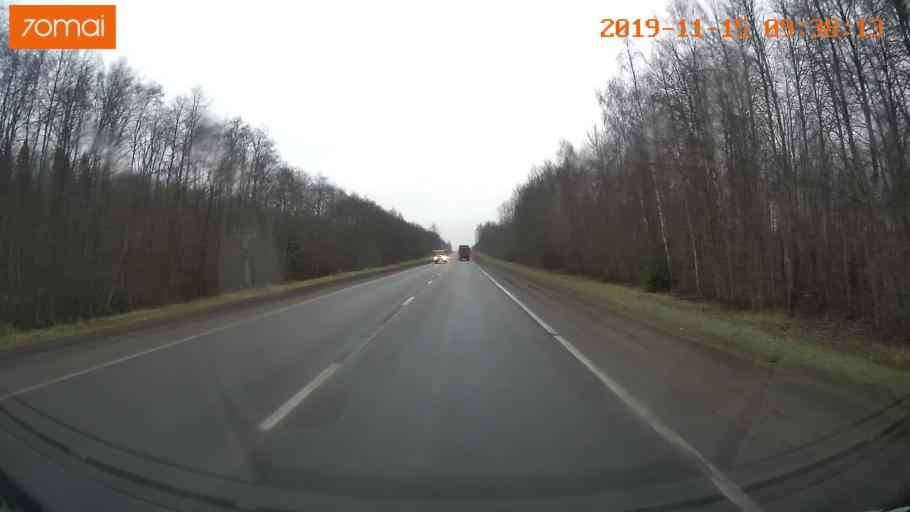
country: RU
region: Vologda
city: Sheksna
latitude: 59.2340
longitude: 38.4513
